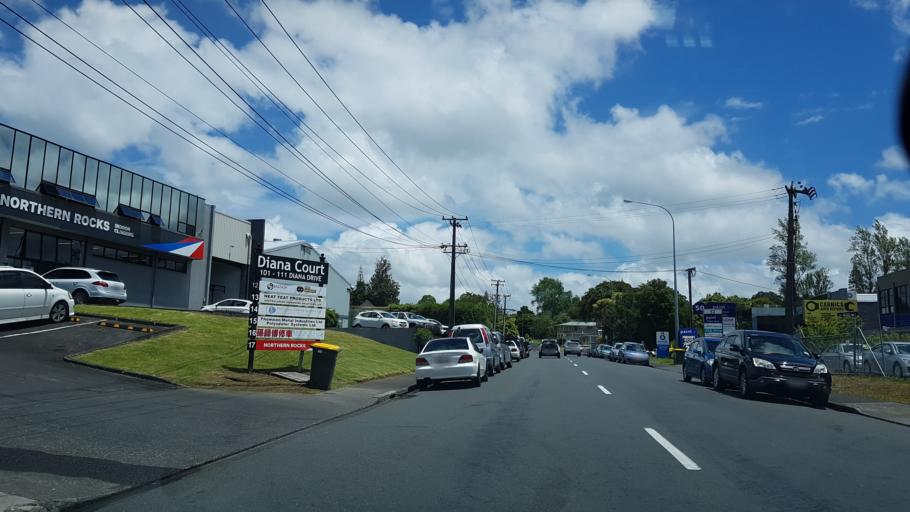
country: NZ
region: Auckland
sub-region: Auckland
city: North Shore
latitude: -36.7753
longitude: 174.7330
